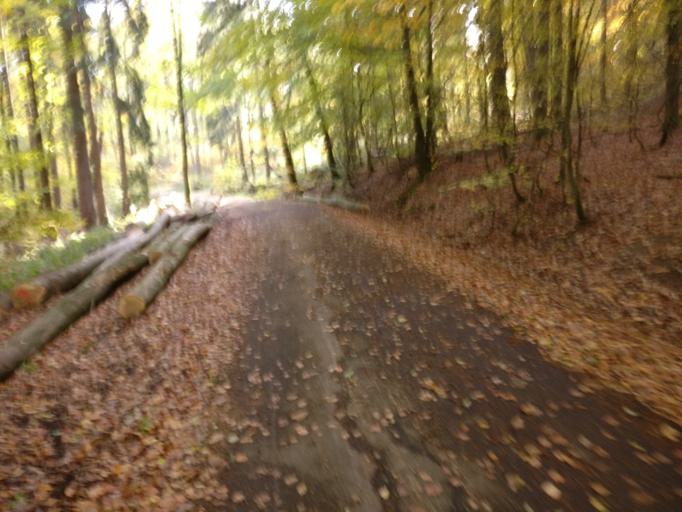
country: DE
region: Hesse
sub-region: Regierungsbezirk Giessen
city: Greifenstein
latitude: 50.6167
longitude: 8.2881
